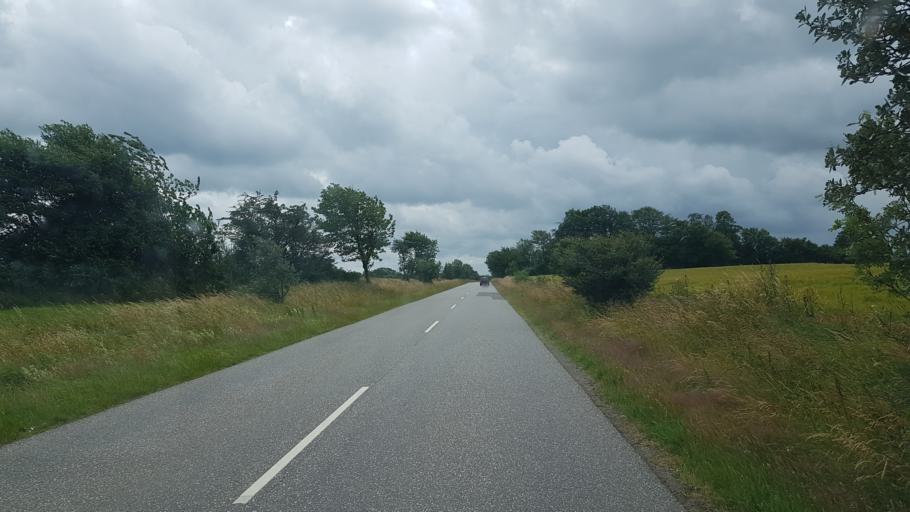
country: DK
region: South Denmark
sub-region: Kolding Kommune
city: Vamdrup
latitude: 55.4489
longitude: 9.2735
